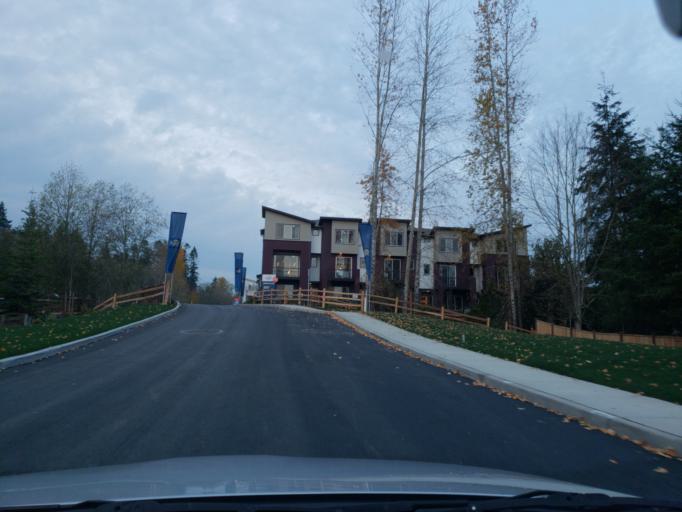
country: US
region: Washington
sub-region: King County
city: Bothell
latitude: 47.7809
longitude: -122.2238
